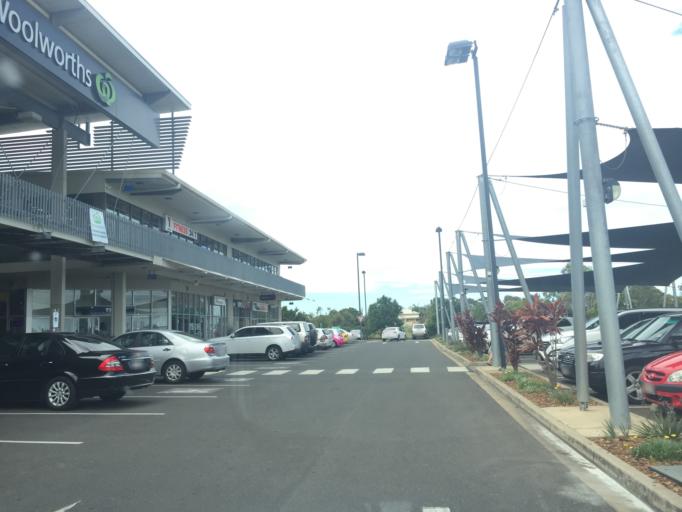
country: AU
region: Queensland
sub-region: Bundaberg
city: Bundaberg
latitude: -24.8183
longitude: 152.4561
